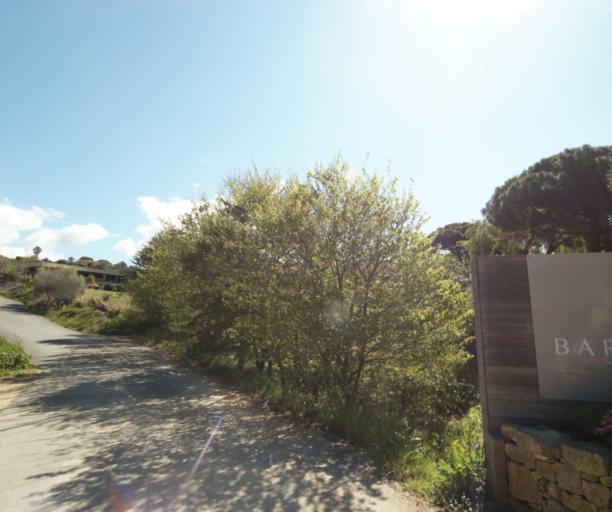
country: FR
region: Corsica
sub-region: Departement de la Corse-du-Sud
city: Propriano
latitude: 41.6789
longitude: 8.9159
